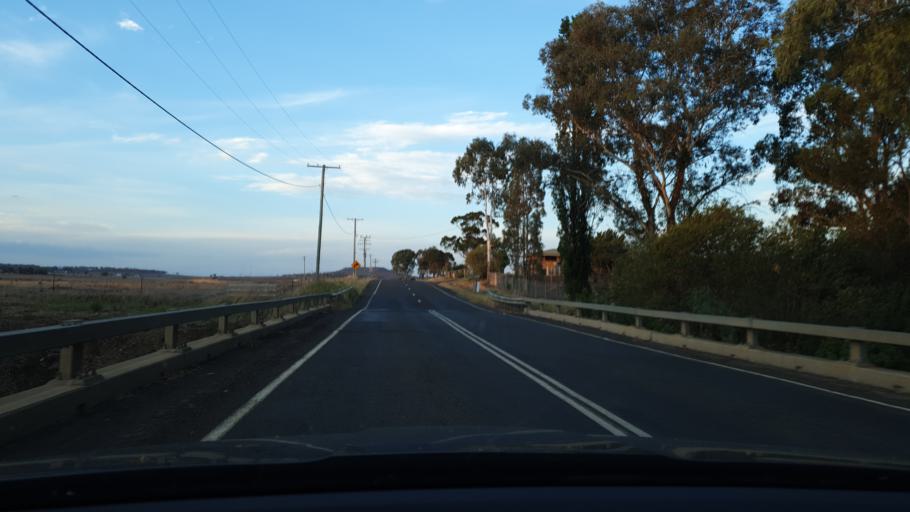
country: AU
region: Queensland
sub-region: Southern Downs
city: Warwick
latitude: -28.0282
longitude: 151.9828
